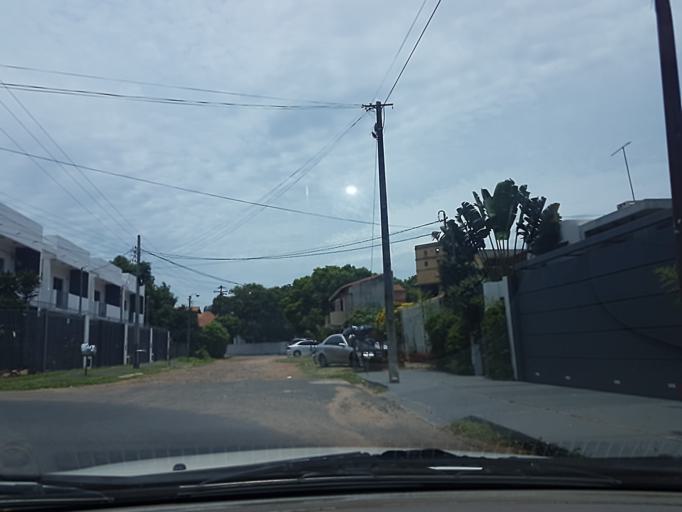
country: PY
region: Central
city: Fernando de la Mora
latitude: -25.2533
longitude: -57.5124
